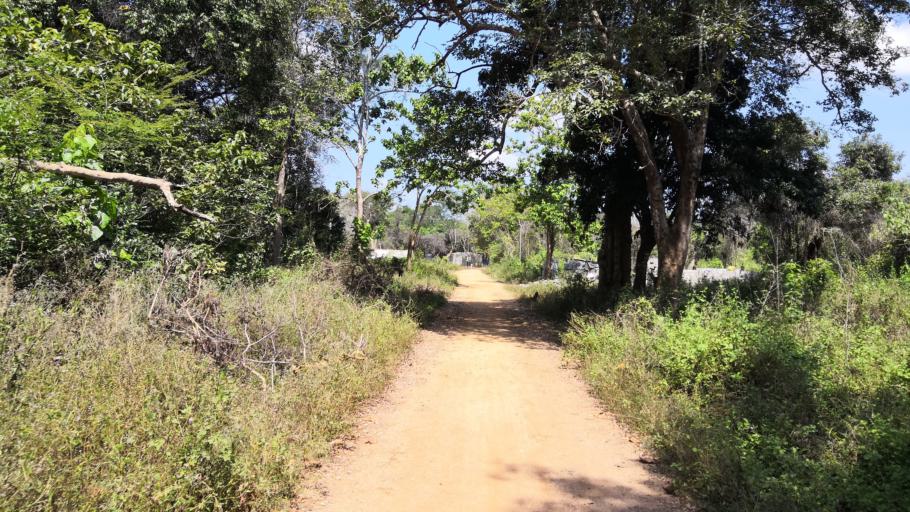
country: LK
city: Padaviya Divisional Secretariat
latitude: 8.9645
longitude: 80.6893
